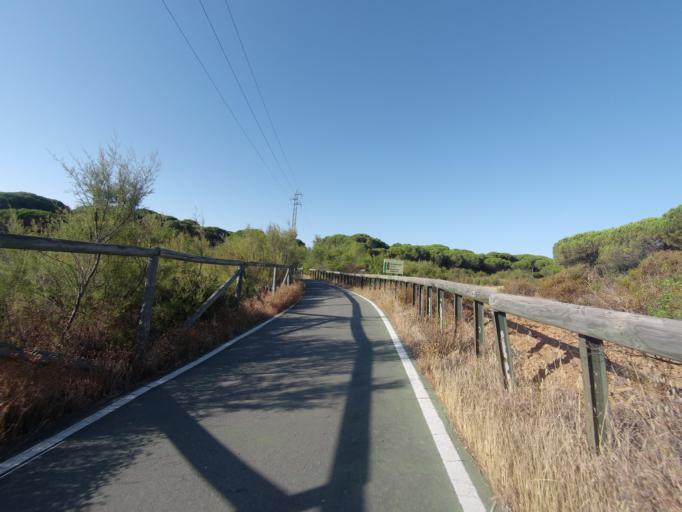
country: ES
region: Andalusia
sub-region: Provincia de Huelva
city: Aljaraque
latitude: 37.2162
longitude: -7.0267
